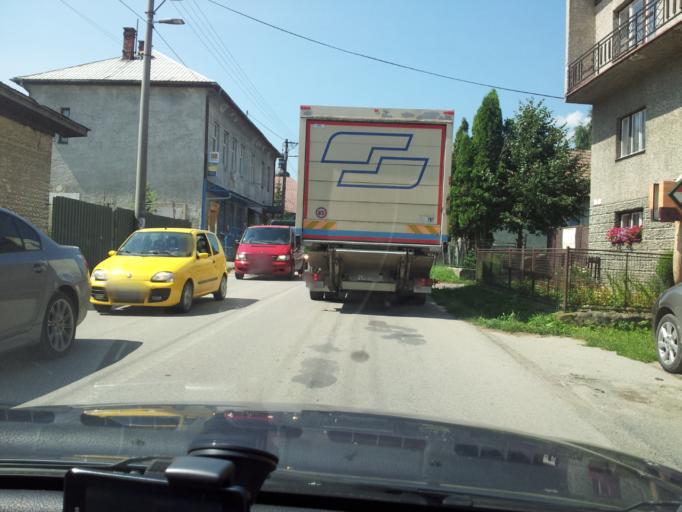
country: SK
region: Zilinsky
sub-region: Okres Dolny Kubin
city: Dolny Kubin
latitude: 49.3254
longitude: 19.3510
